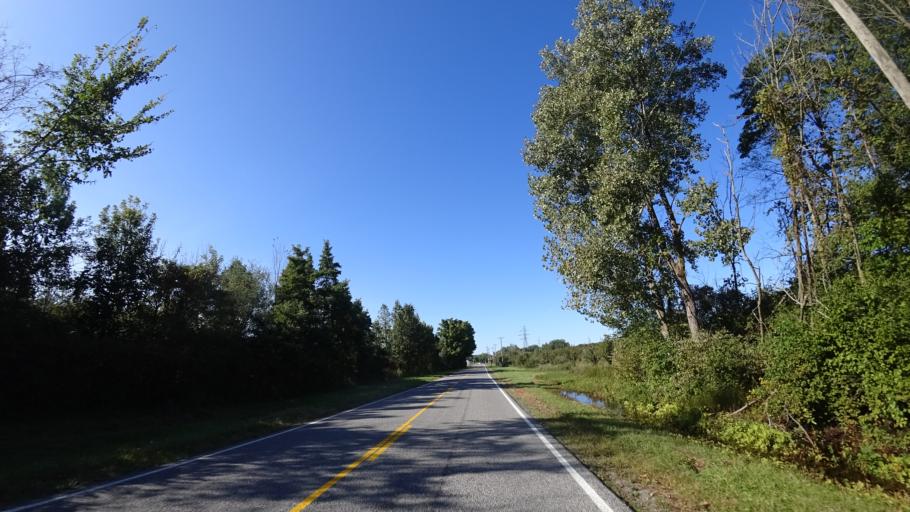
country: US
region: Michigan
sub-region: Berrien County
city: Benton Heights
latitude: 42.1487
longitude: -86.4279
